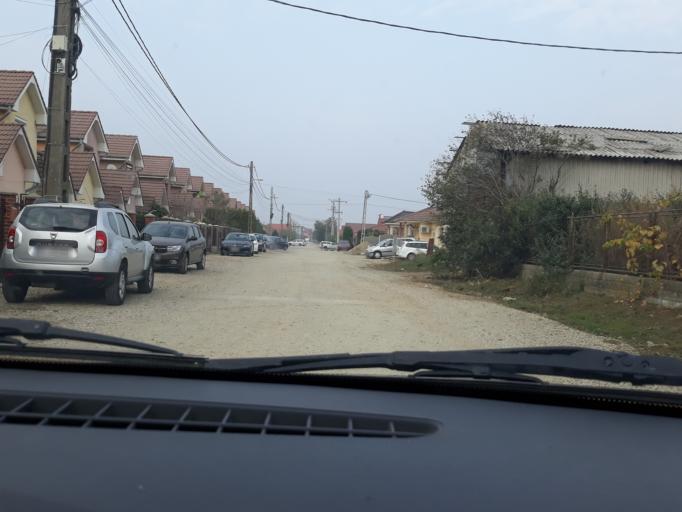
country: RO
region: Bihor
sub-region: Comuna Santandrei
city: Santandrei
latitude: 47.0620
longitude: 21.8506
